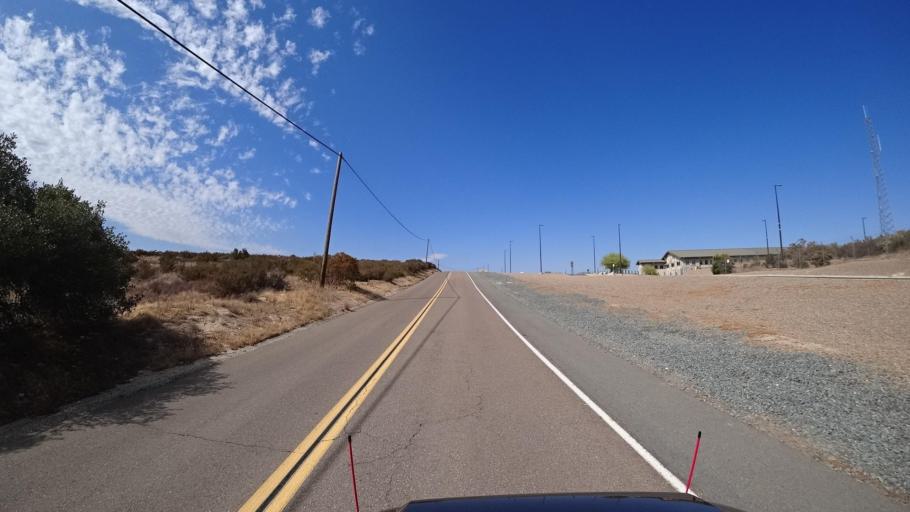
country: US
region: California
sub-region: San Diego County
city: Campo
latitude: 32.6810
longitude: -116.2926
